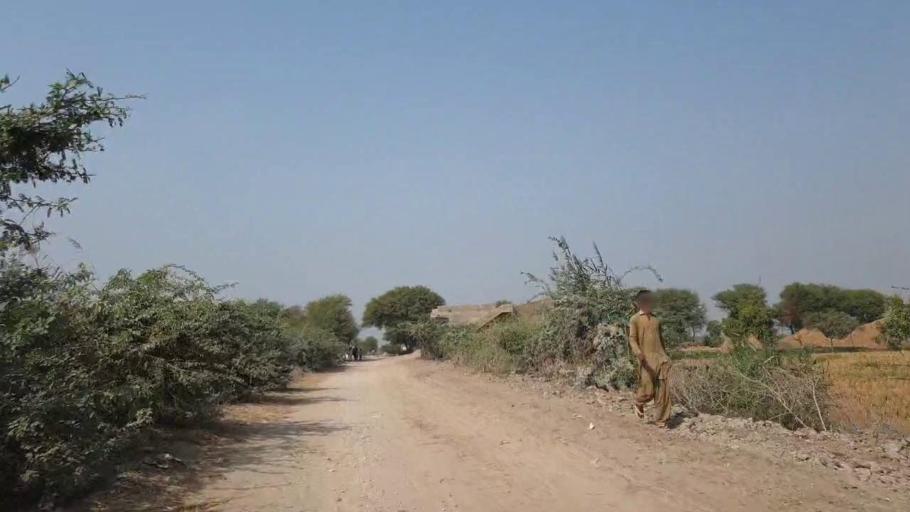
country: PK
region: Sindh
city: Kario
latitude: 24.9309
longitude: 68.5594
